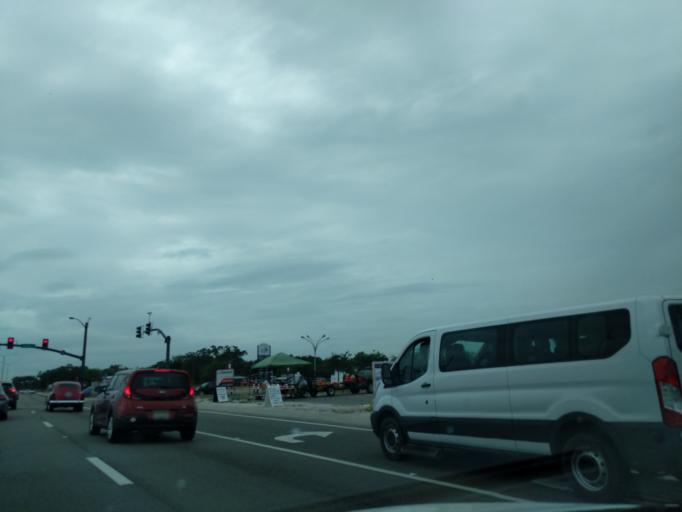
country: US
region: Mississippi
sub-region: Harrison County
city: Long Beach
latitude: 30.3452
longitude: -89.1474
